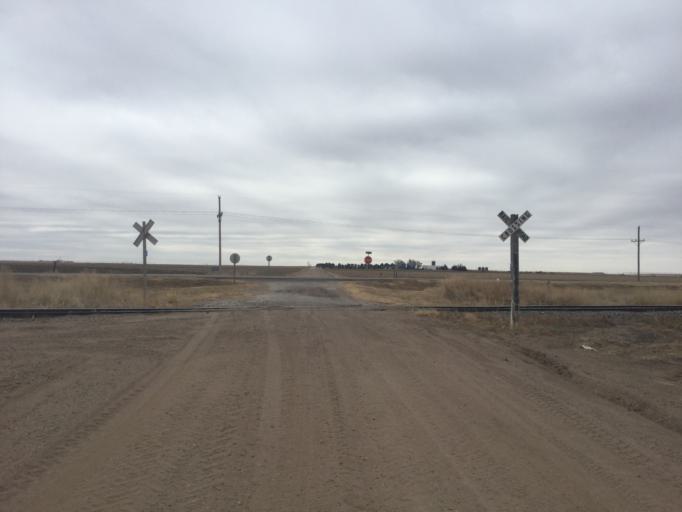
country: US
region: Kansas
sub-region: Haskell County
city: Sublette
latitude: 37.5221
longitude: -100.7072
